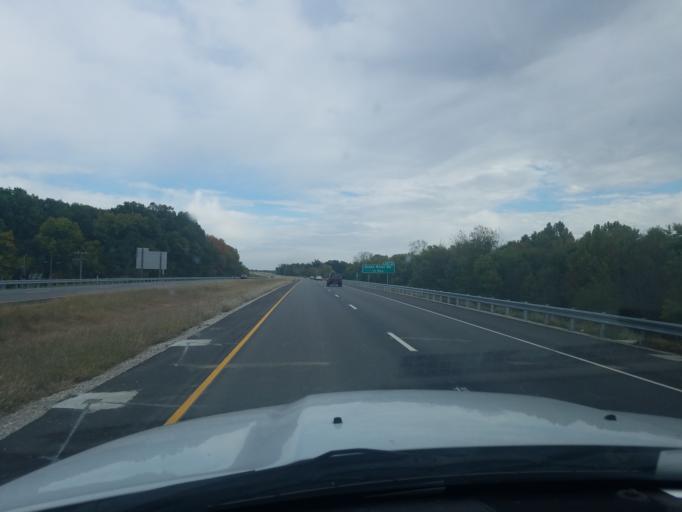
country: US
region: Indiana
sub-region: Vanderburgh County
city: Evansville
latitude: 37.9393
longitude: -87.5065
